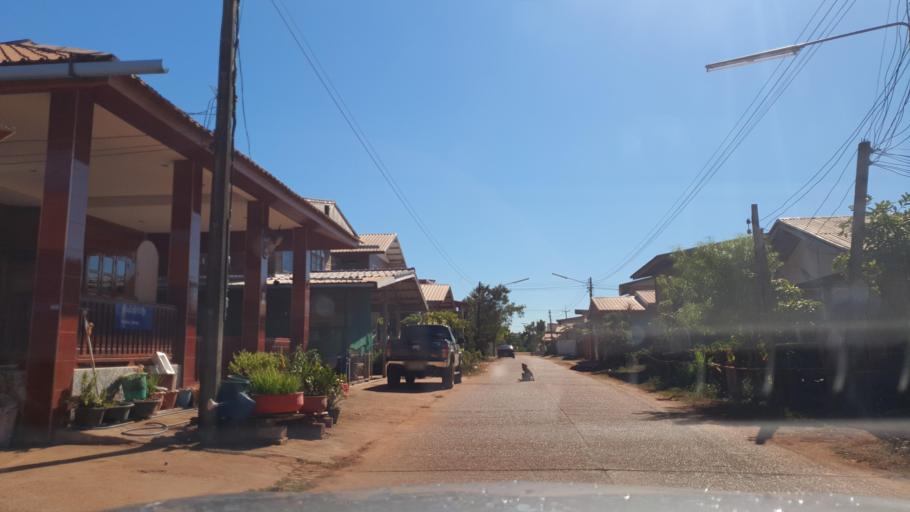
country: TH
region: Nakhon Phanom
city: Ban Phaeng
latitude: 17.8294
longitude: 104.2663
